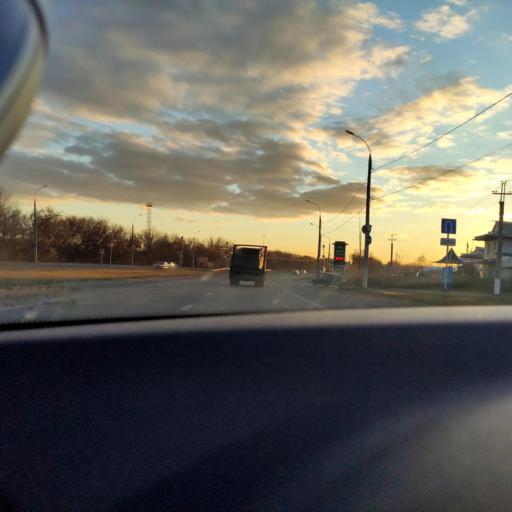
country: RU
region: Samara
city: Smyshlyayevka
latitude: 53.2571
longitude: 50.3735
